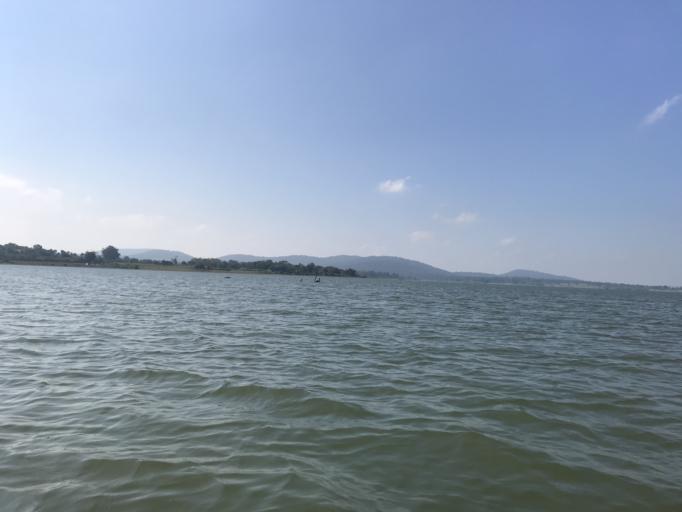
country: IN
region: Karnataka
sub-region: Mysore
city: Sargur
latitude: 11.9365
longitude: 76.2711
